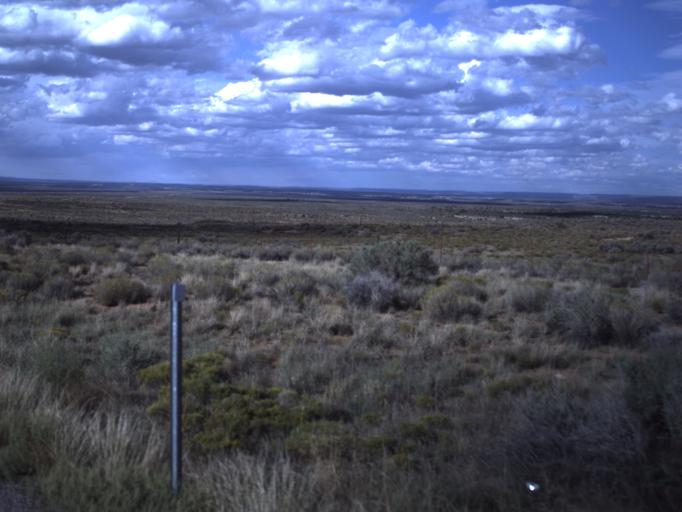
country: US
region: Utah
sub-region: San Juan County
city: Blanding
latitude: 37.3350
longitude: -109.3475
